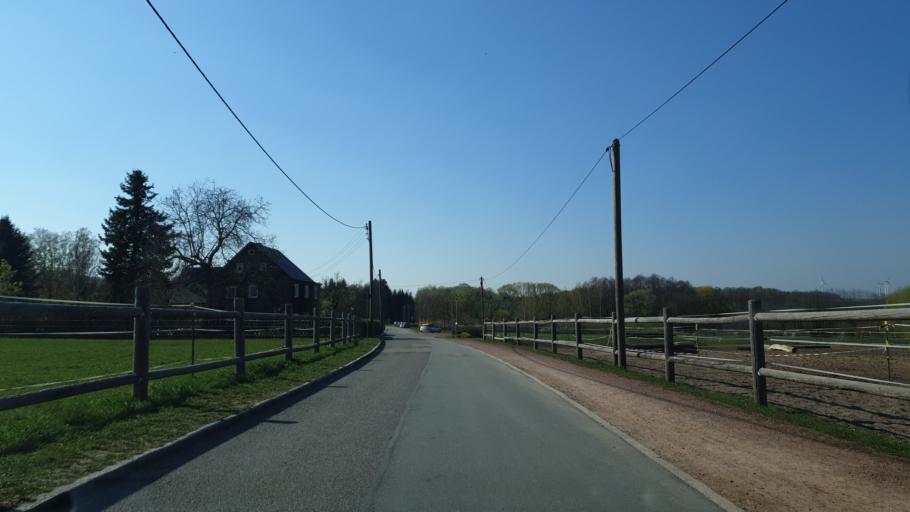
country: DE
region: Saxony
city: Oelsnitz
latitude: 50.7330
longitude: 12.7003
